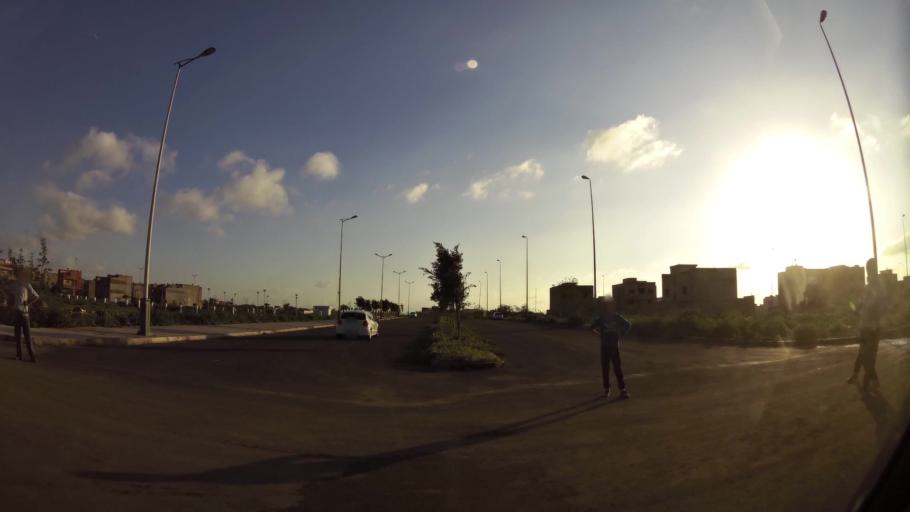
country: MA
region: Chaouia-Ouardigha
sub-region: Settat Province
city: Settat
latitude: 33.0116
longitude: -7.5978
